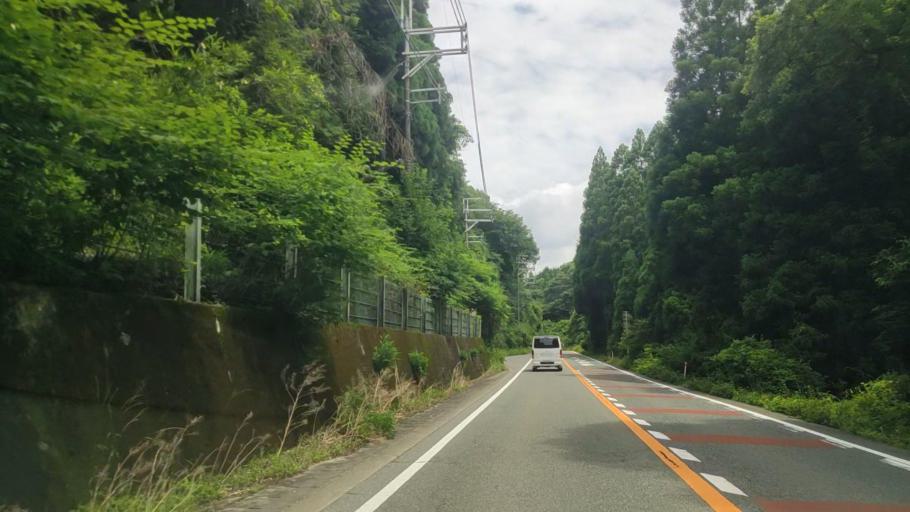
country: JP
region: Hyogo
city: Yamazakicho-nakabirose
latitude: 34.9906
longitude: 134.4072
